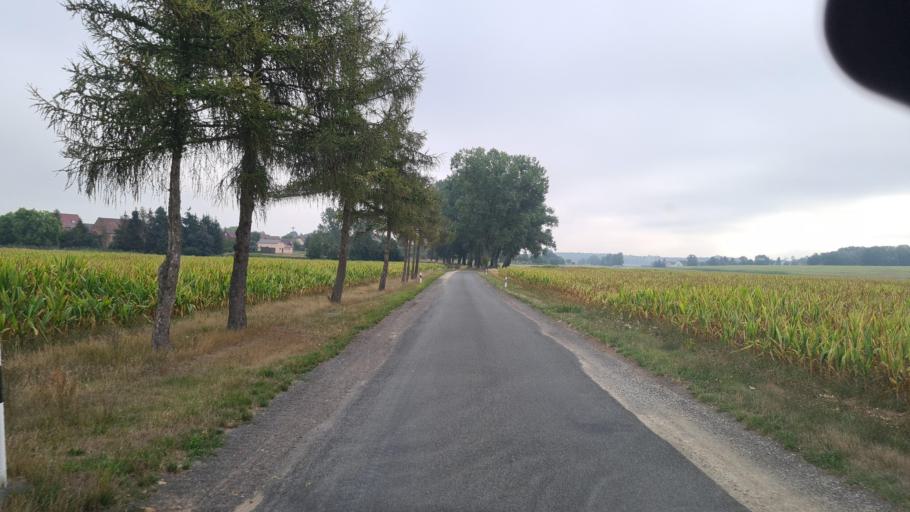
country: DE
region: Brandenburg
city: Niemegk
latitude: 52.0781
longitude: 12.6344
